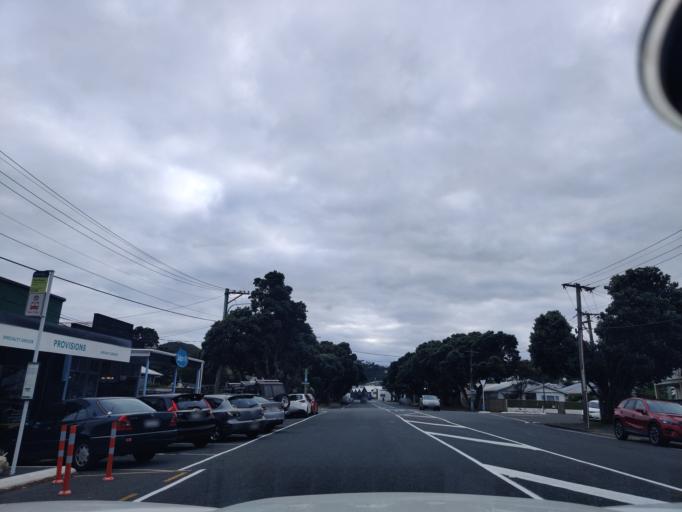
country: NZ
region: Wellington
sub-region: Wellington City
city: Wellington
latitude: -41.3120
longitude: 174.8195
